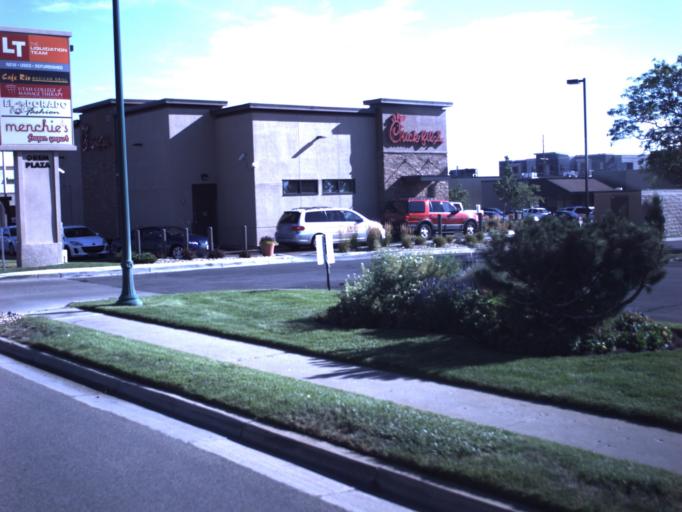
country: US
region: Utah
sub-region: Utah County
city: Orem
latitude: 40.3001
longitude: -111.6965
